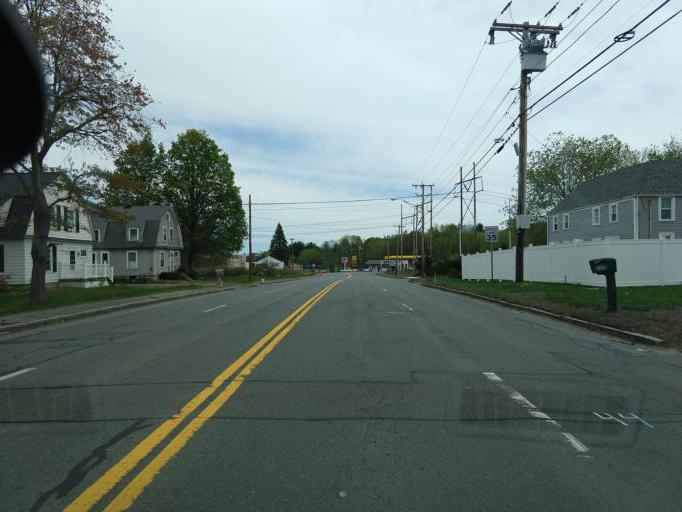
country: US
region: Massachusetts
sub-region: Essex County
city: Haverhill
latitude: 42.7419
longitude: -71.1112
